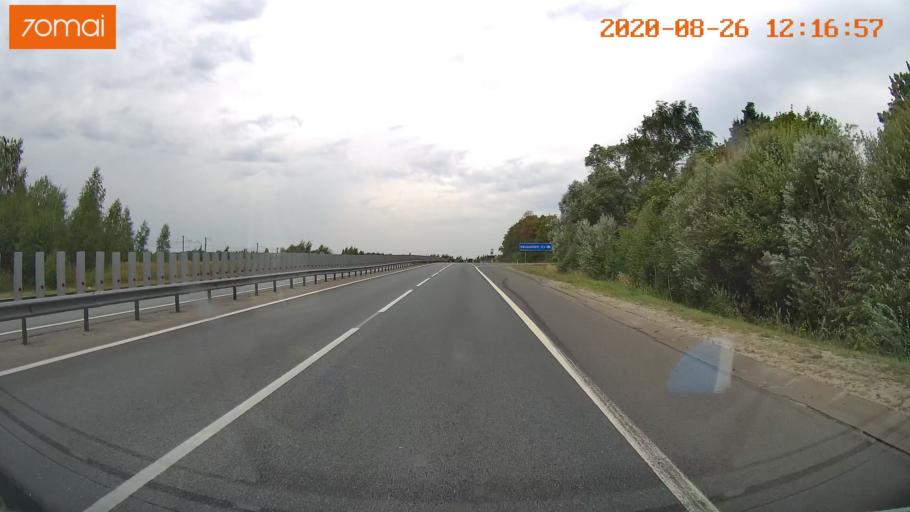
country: RU
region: Rjazan
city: Murmino
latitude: 54.4539
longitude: 40.0338
